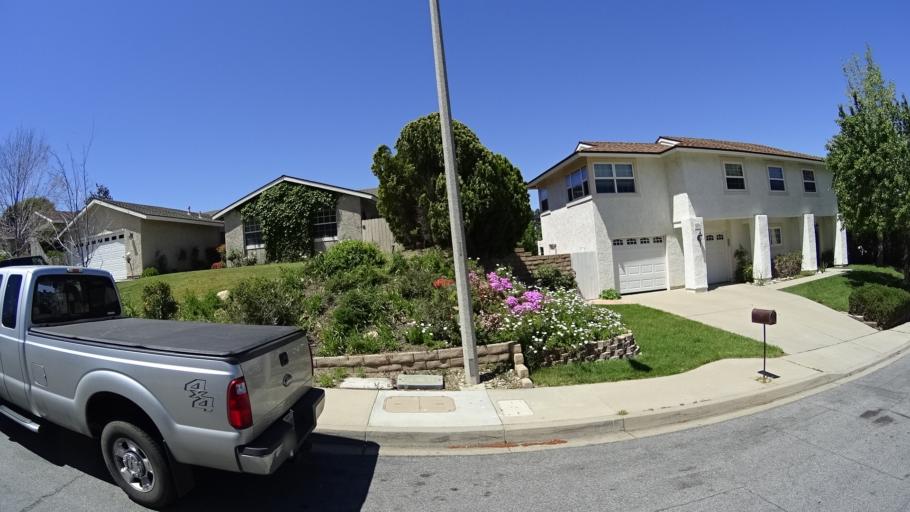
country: US
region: California
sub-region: Ventura County
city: Casa Conejo
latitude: 34.1759
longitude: -118.9001
